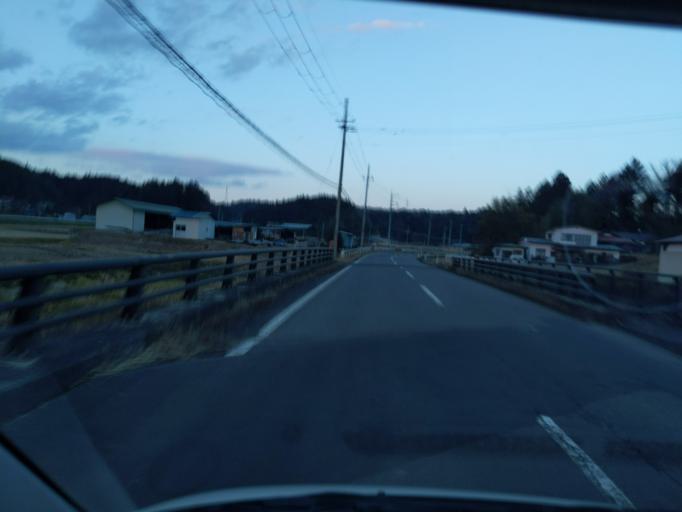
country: JP
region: Iwate
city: Ichinoseki
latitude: 38.8056
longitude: 141.1170
